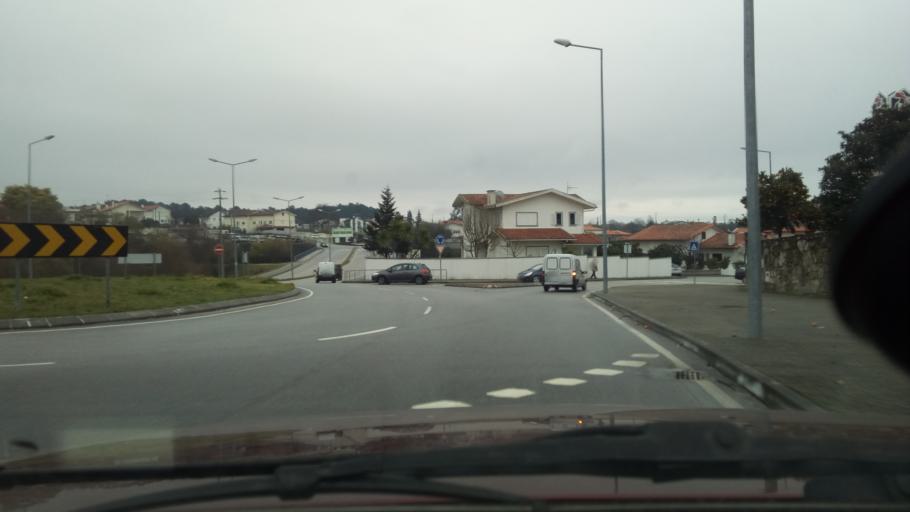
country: PT
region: Viseu
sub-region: Viseu
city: Rio de Loba
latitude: 40.6472
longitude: -7.8716
